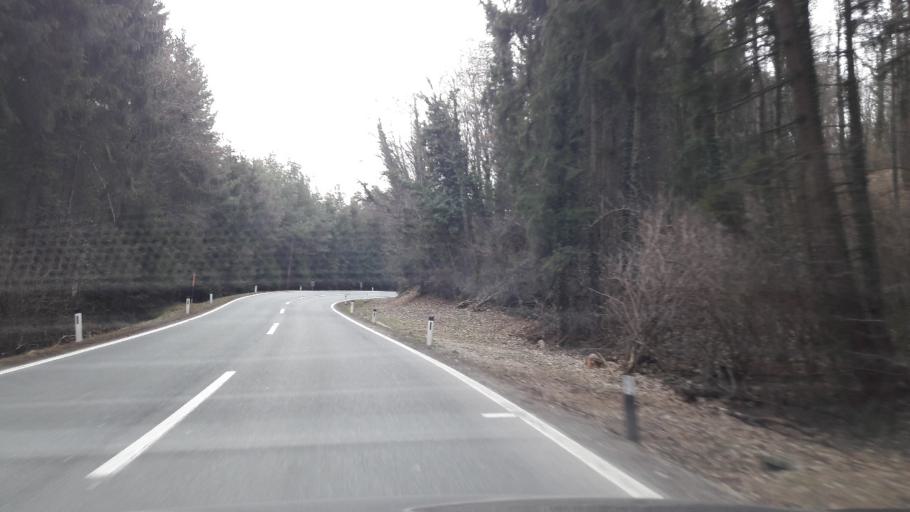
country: AT
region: Styria
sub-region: Politischer Bezirk Graz-Umgebung
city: Thal
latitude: 47.0638
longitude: 15.3288
